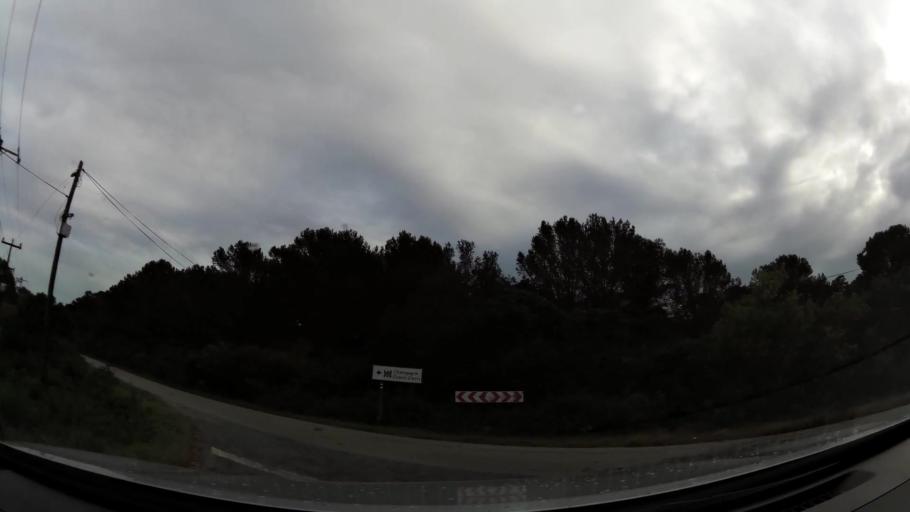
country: ZA
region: Eastern Cape
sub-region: Nelson Mandela Bay Metropolitan Municipality
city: Port Elizabeth
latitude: -34.0084
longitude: 25.4908
